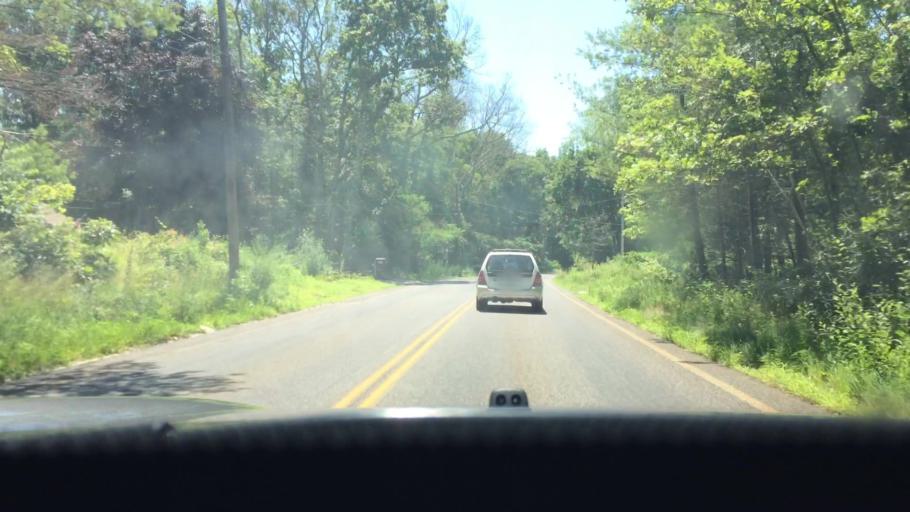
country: US
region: Rhode Island
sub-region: Providence County
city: Harrisville
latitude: 42.0159
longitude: -71.6761
